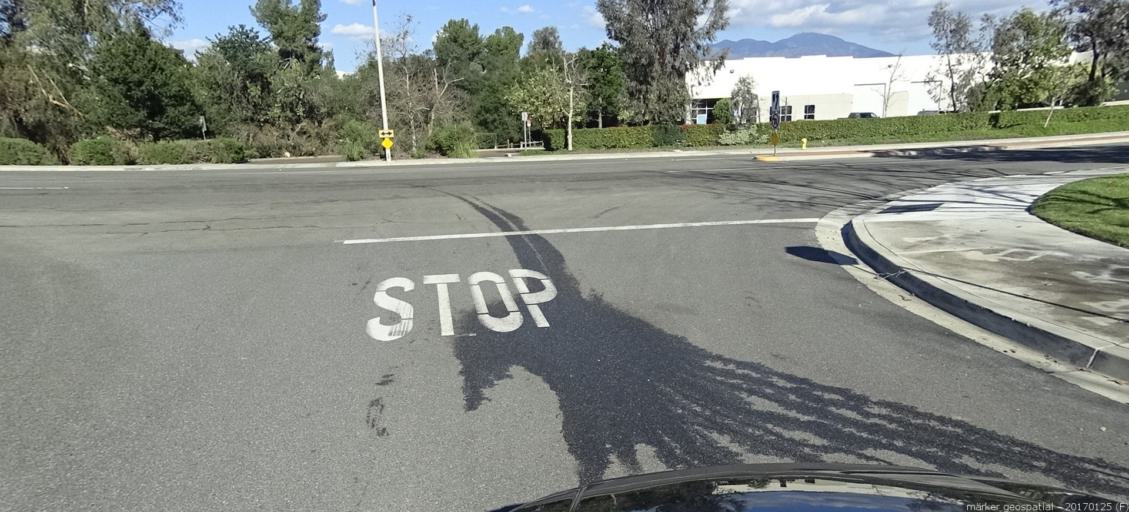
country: US
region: California
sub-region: Orange County
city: Lake Forest
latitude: 33.6621
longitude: -117.6732
